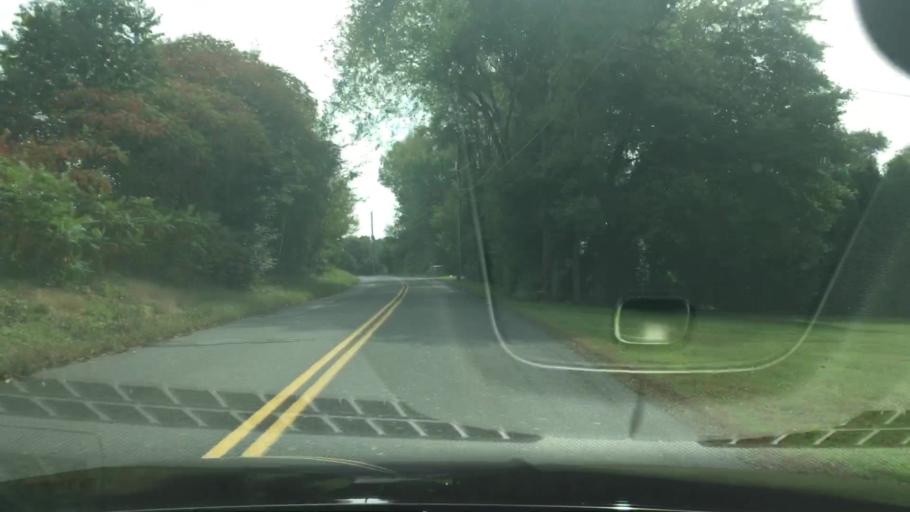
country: US
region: Connecticut
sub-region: Hartford County
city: Hazardville
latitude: 42.0004
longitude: -72.5055
